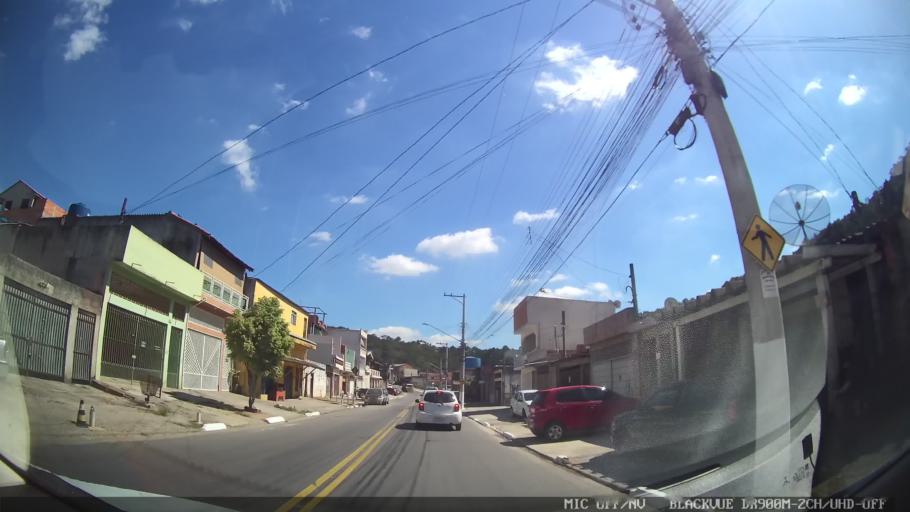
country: BR
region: Sao Paulo
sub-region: Cajamar
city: Cajamar
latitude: -23.4245
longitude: -46.8274
